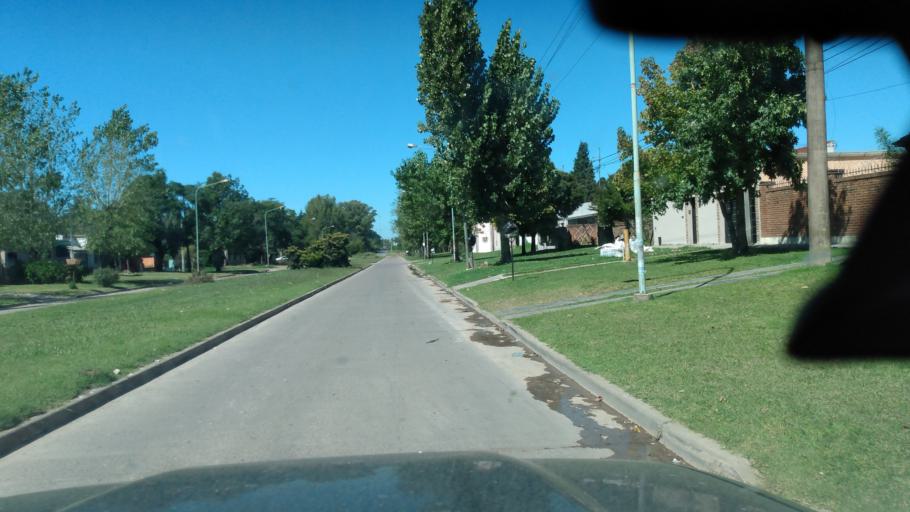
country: AR
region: Buenos Aires
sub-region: Partido de Lujan
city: Lujan
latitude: -34.5695
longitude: -59.1321
